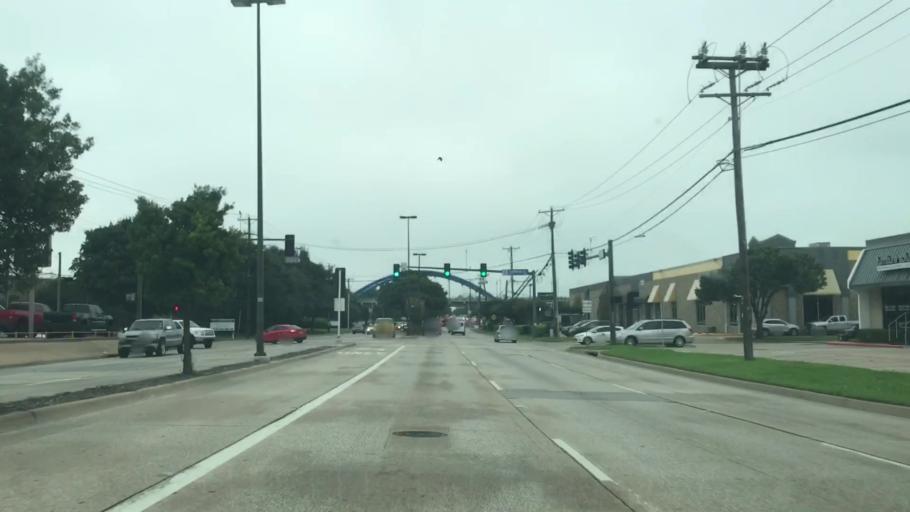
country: US
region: Texas
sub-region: Dallas County
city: Addison
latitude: 32.9586
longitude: -96.8386
